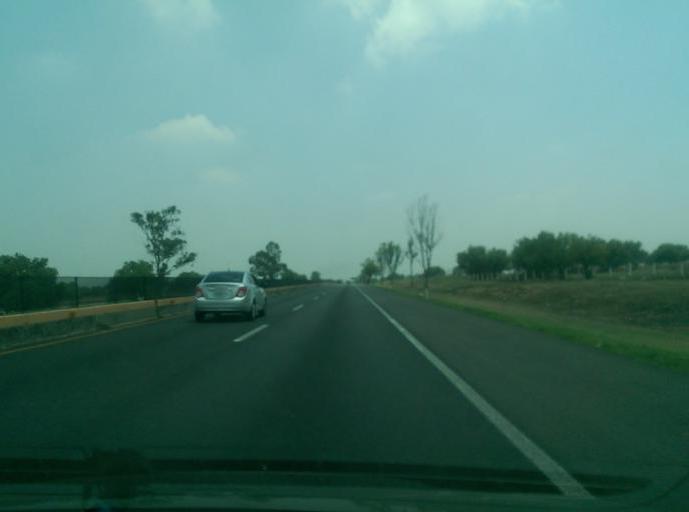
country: MX
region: Mexico
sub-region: Zumpango
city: Ex-Hacienda de Guadalupe
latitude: 19.7865
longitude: -98.9480
